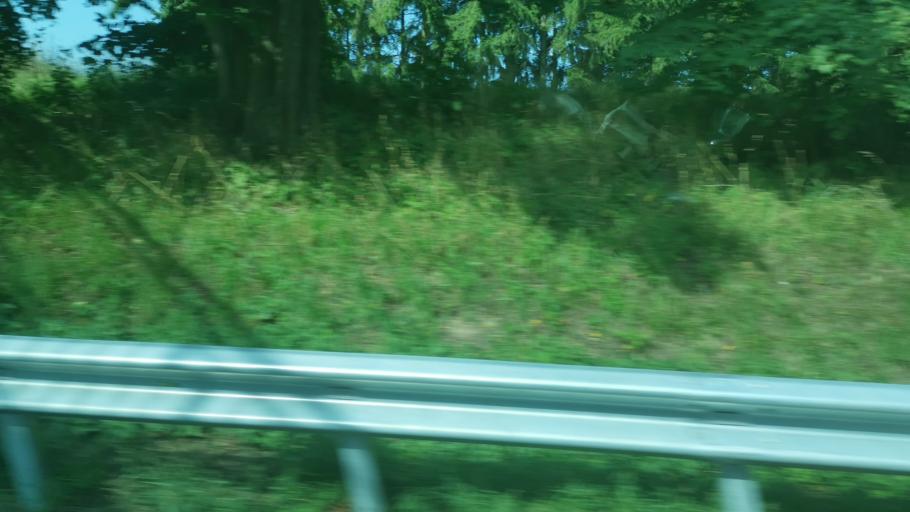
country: DE
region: Bavaria
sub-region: Upper Palatinate
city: Willmering
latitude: 49.2377
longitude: 12.6752
